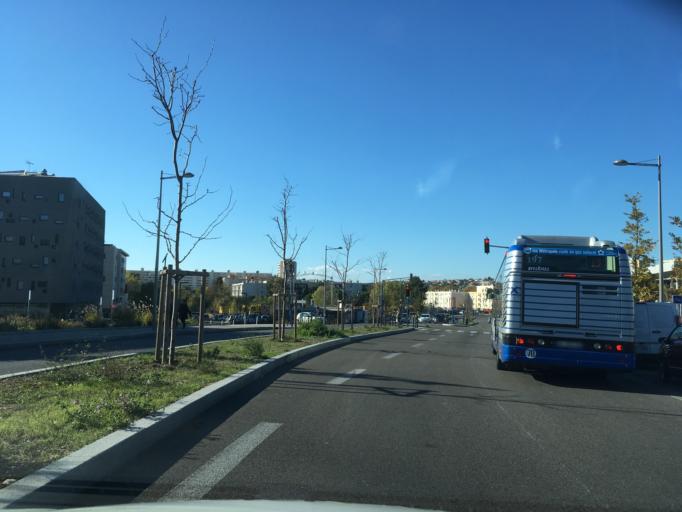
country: FR
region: Languedoc-Roussillon
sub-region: Departement de l'Herault
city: Juvignac
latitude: 43.6257
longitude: 3.8247
